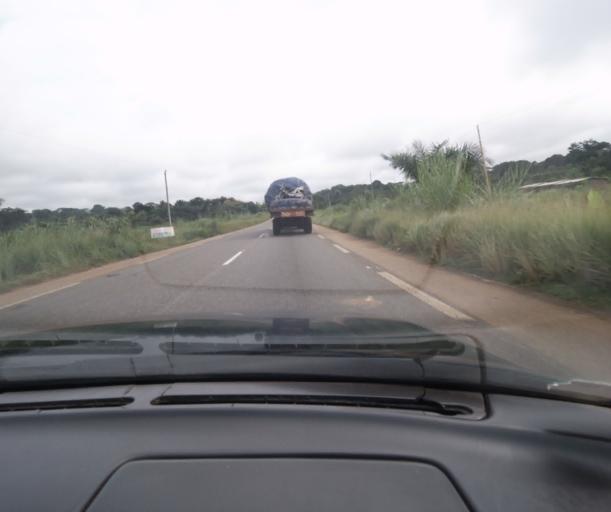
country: CM
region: Centre
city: Ombesa
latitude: 4.5814
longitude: 11.2657
